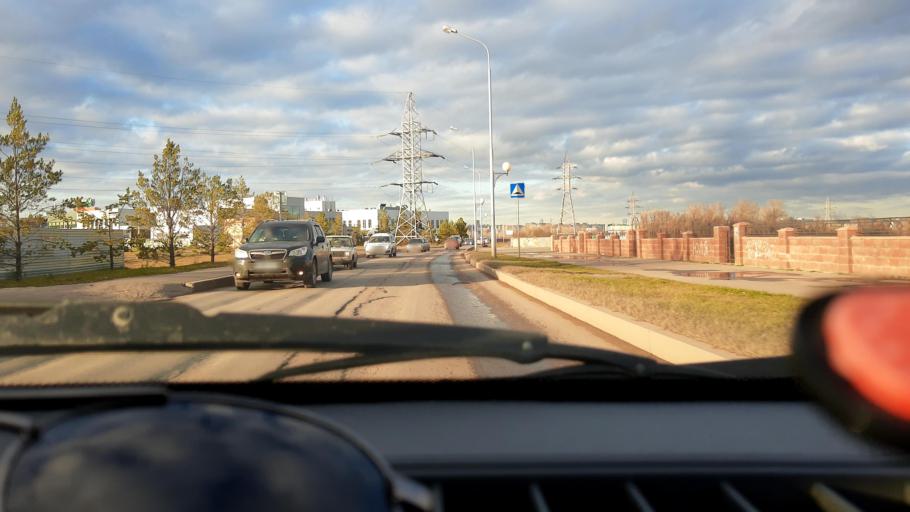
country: RU
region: Bashkortostan
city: Ufa
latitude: 54.7815
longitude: 56.0774
